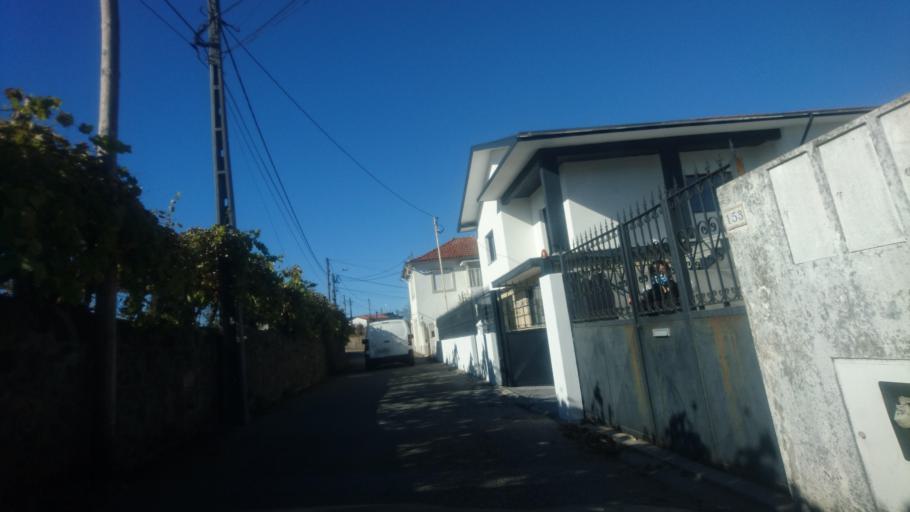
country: PT
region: Aveiro
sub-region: Oliveira de Azemeis
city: Sao Roque
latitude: 40.8835
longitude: -8.4566
